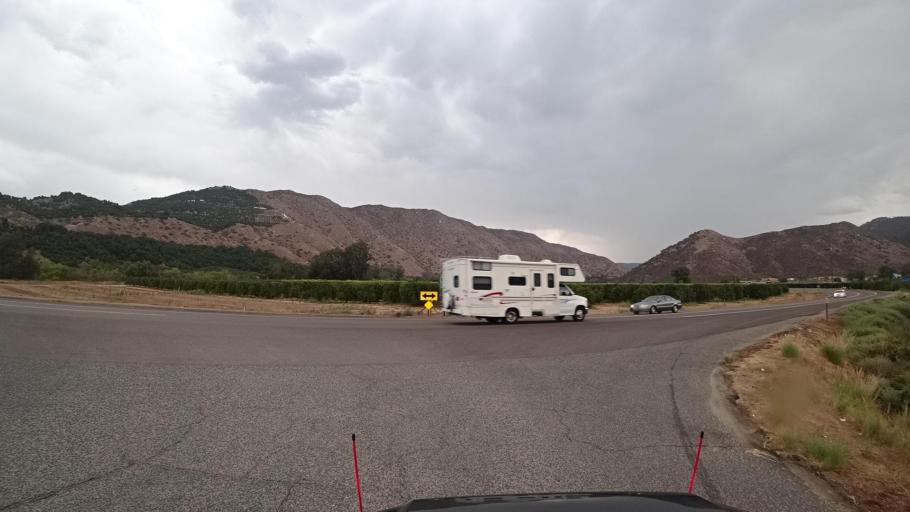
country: US
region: California
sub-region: San Diego County
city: San Pasqual
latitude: 33.0918
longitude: -116.9546
